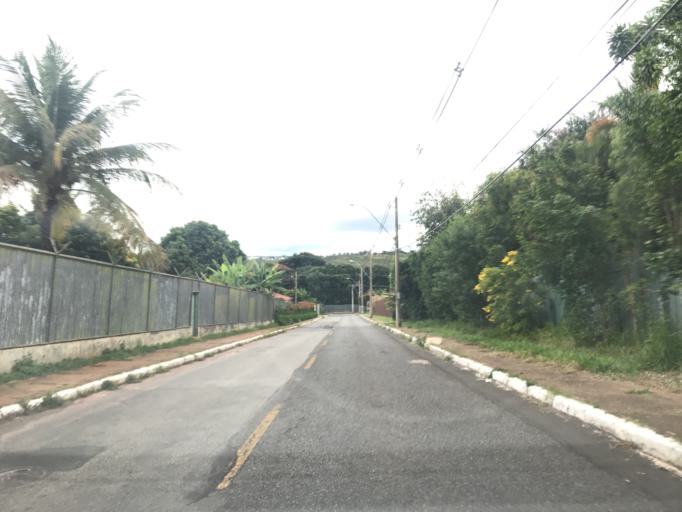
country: BR
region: Federal District
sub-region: Brasilia
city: Brasilia
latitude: -15.7210
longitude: -47.8767
